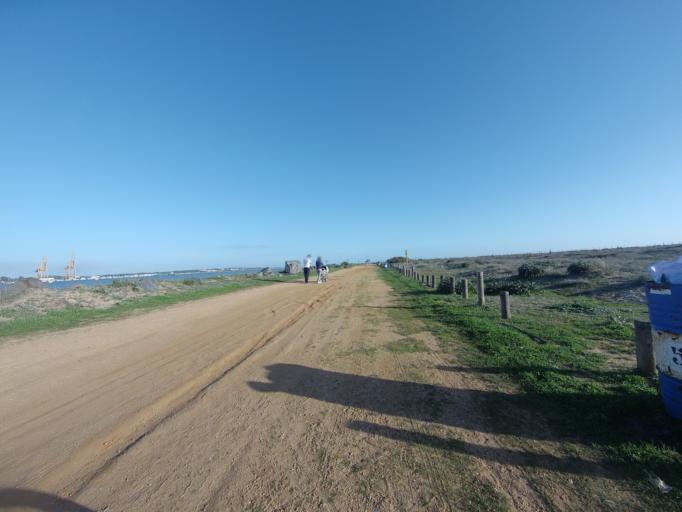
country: ES
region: Andalusia
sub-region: Provincia de Huelva
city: Punta Umbria
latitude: 37.1476
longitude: -6.8924
